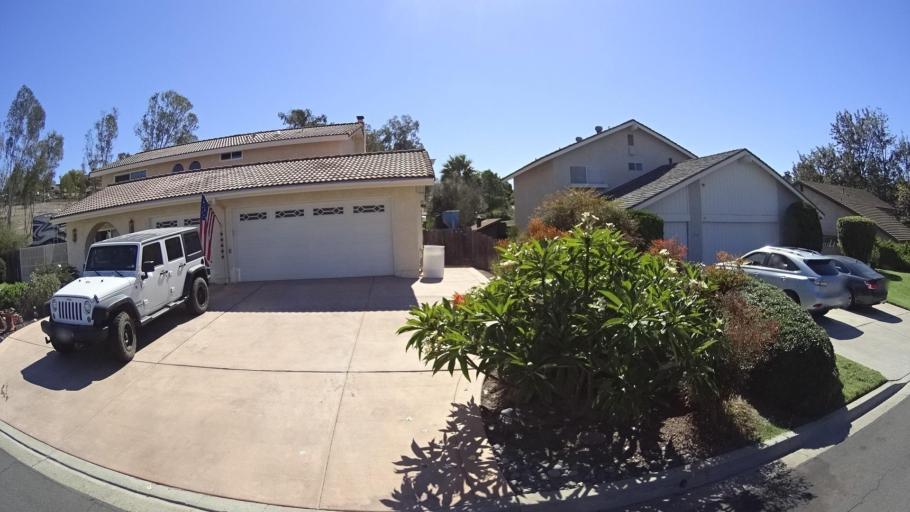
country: US
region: California
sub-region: San Diego County
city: Bonita
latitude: 32.6716
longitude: -117.0029
